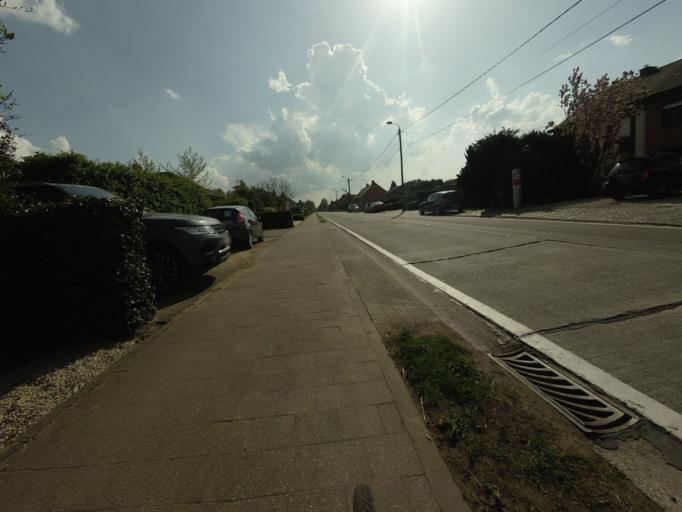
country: BE
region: Flanders
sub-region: Provincie Antwerpen
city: Putte
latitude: 51.0654
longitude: 4.6388
